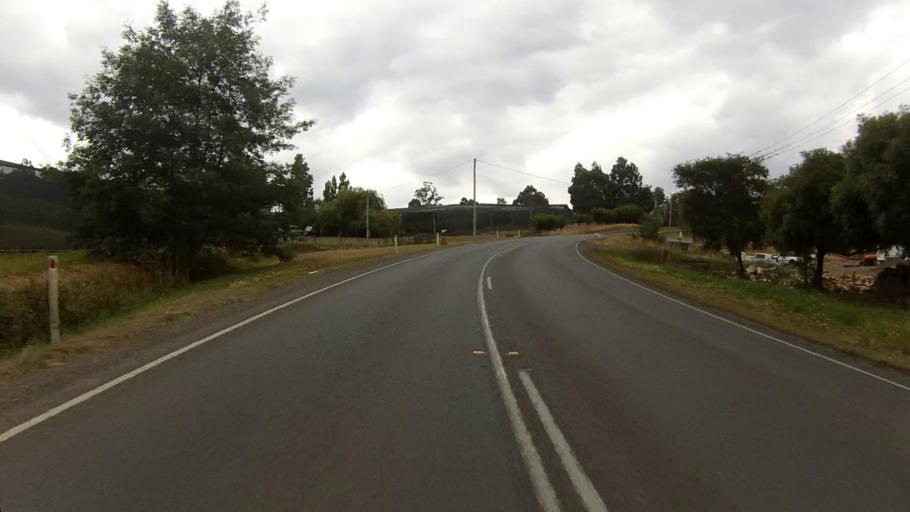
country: AU
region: Tasmania
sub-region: Huon Valley
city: Cygnet
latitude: -43.1306
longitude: 147.0476
